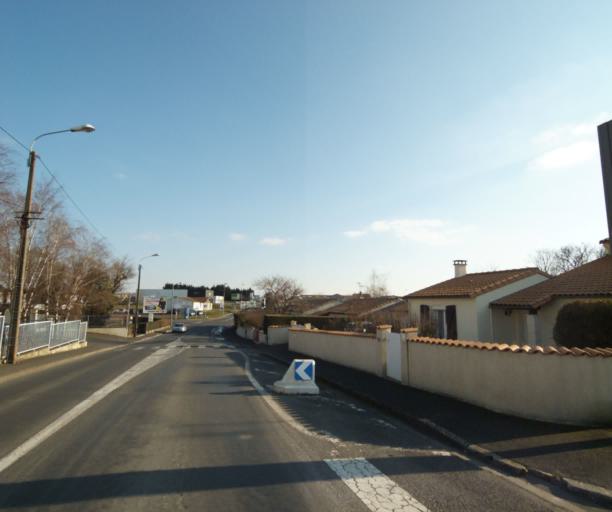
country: FR
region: Poitou-Charentes
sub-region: Departement des Deux-Sevres
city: Niort
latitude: 46.3340
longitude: -0.4232
